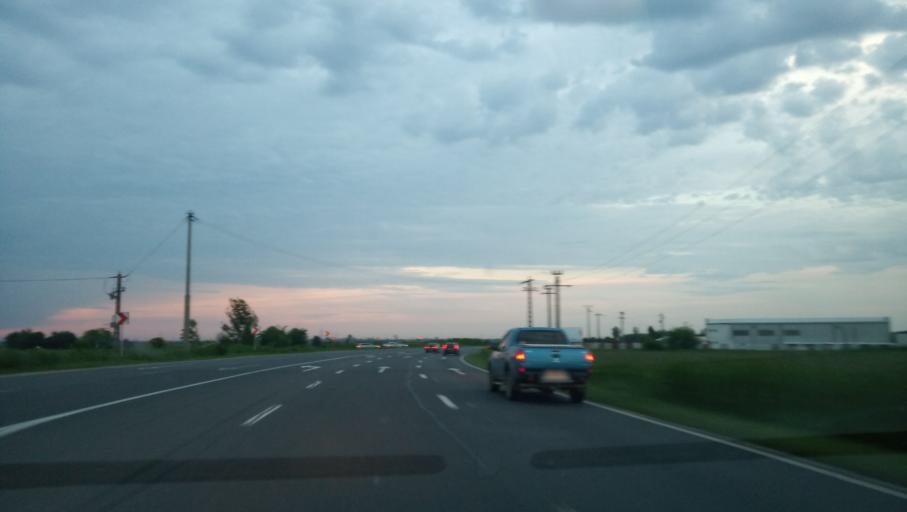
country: RO
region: Timis
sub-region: Comuna Sag
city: Sag
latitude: 45.6824
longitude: 21.1687
